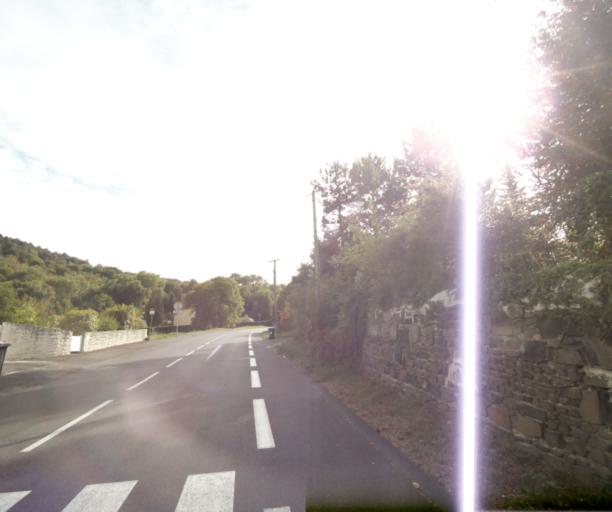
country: FR
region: Auvergne
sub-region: Departement du Puy-de-Dome
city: Romagnat
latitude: 45.7235
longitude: 3.0978
